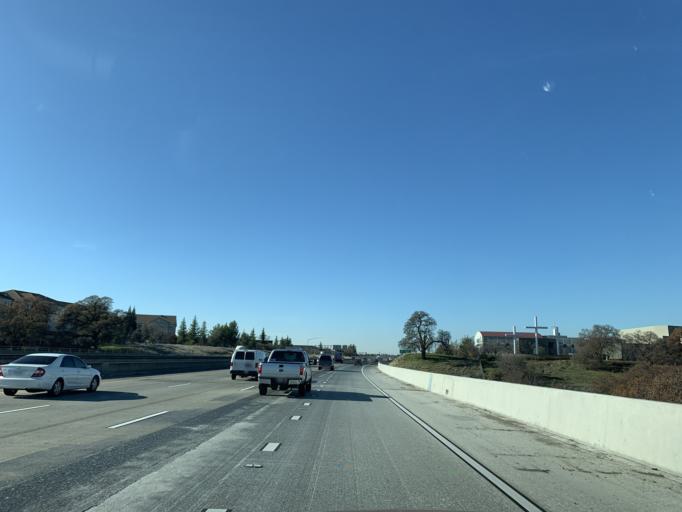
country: US
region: California
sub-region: Placer County
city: Rocklin
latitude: 38.7738
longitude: -121.2566
